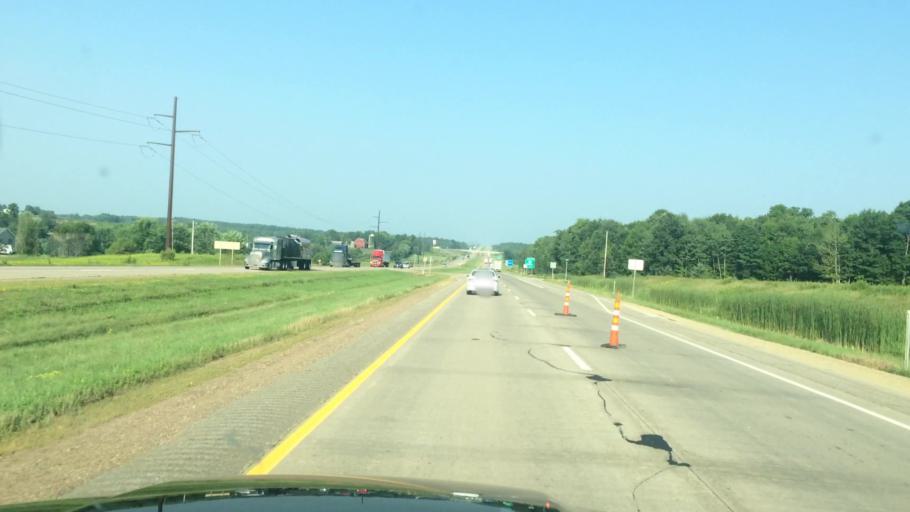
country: US
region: Wisconsin
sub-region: Marathon County
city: Edgar
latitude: 44.9446
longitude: -89.9439
